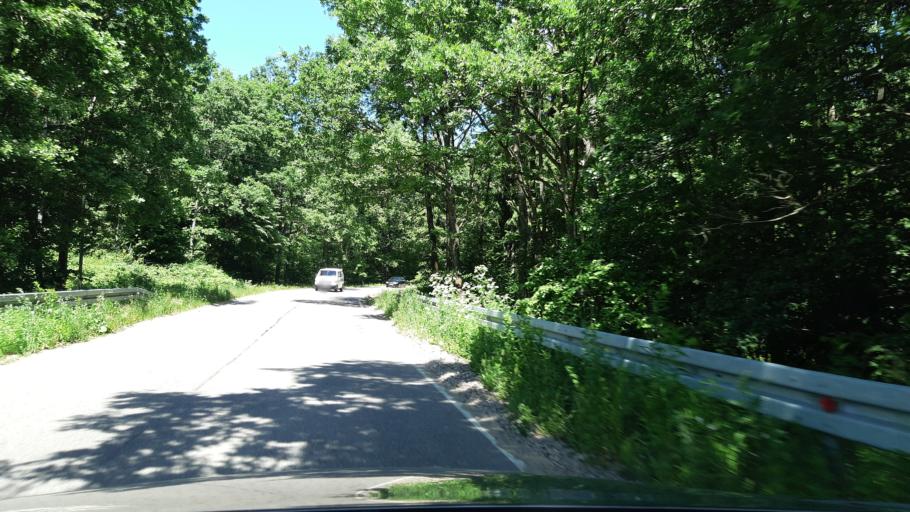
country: PL
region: Warmian-Masurian Voivodeship
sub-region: Powiat piski
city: Ruciane-Nida
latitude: 53.7185
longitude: 21.4963
